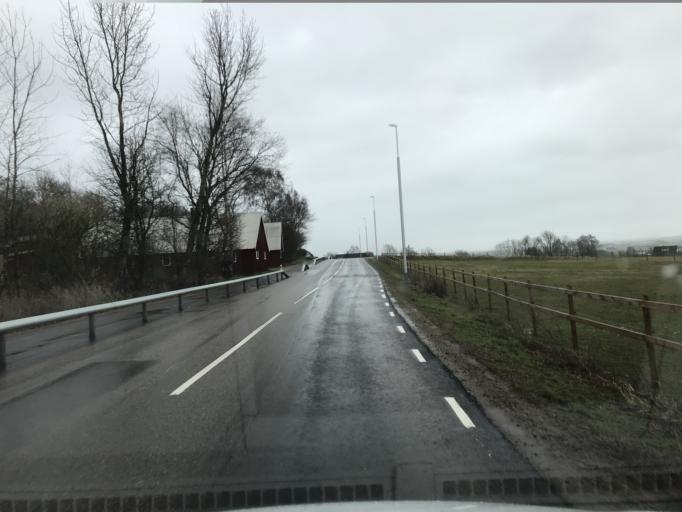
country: SE
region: Skane
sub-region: Bastads Kommun
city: Forslov
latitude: 56.3504
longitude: 12.8501
